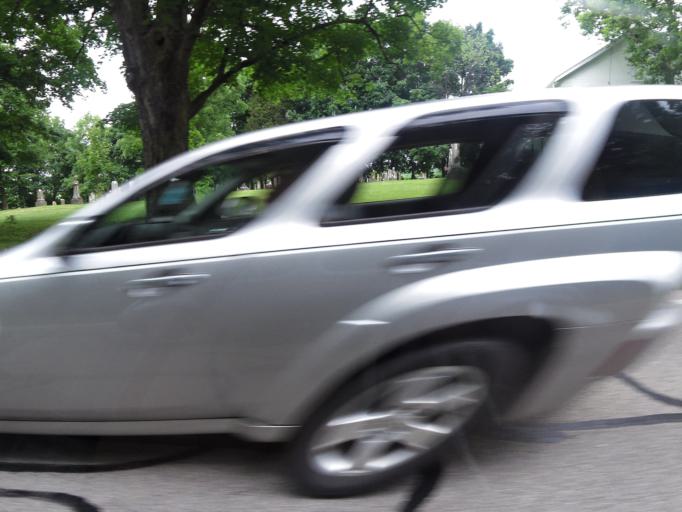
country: US
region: Ohio
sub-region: Warren County
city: Waynesville
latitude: 39.4962
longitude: -83.9805
